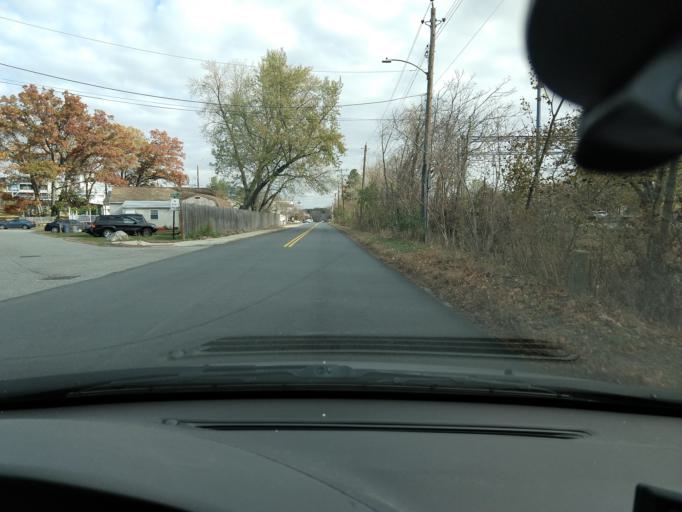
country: US
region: Massachusetts
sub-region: Middlesex County
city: Woburn
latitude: 42.4982
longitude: -71.1669
